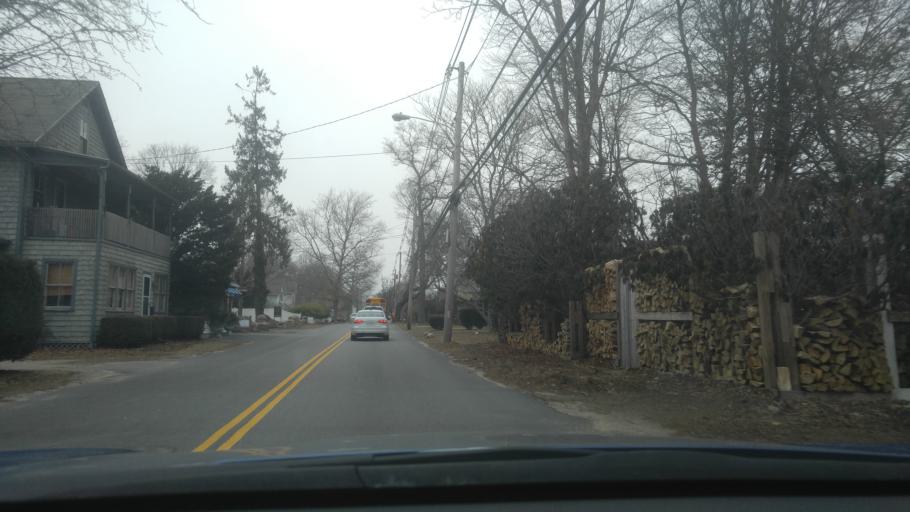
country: US
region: Rhode Island
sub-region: Washington County
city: Wakefield-Peacedale
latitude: 41.4371
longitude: -71.4949
